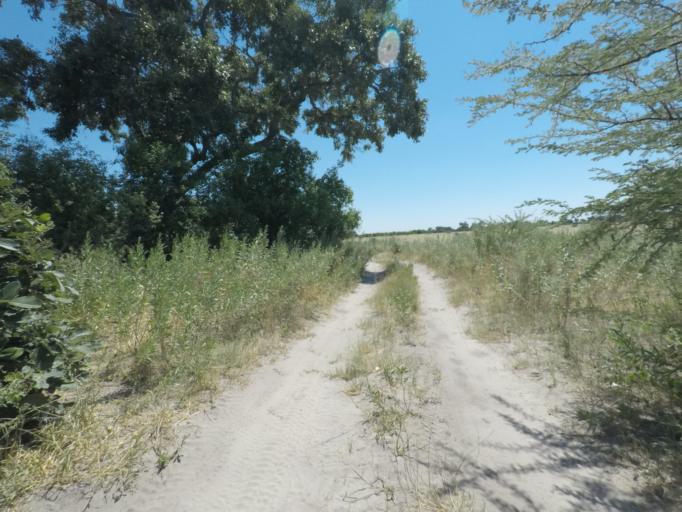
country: BW
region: North West
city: Maun
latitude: -19.4735
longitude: 23.5535
